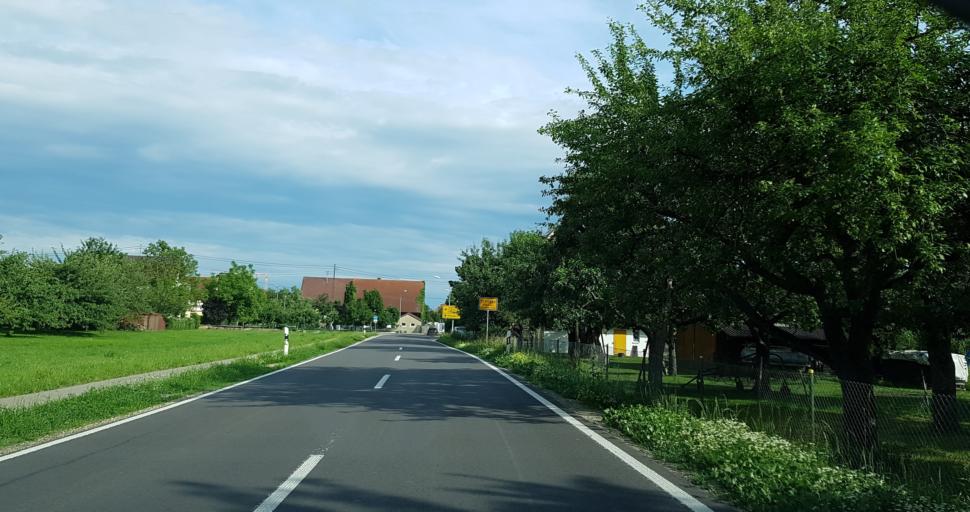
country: DE
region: Baden-Wuerttemberg
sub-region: Tuebingen Region
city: Ersingen
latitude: 48.2932
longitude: 9.8498
